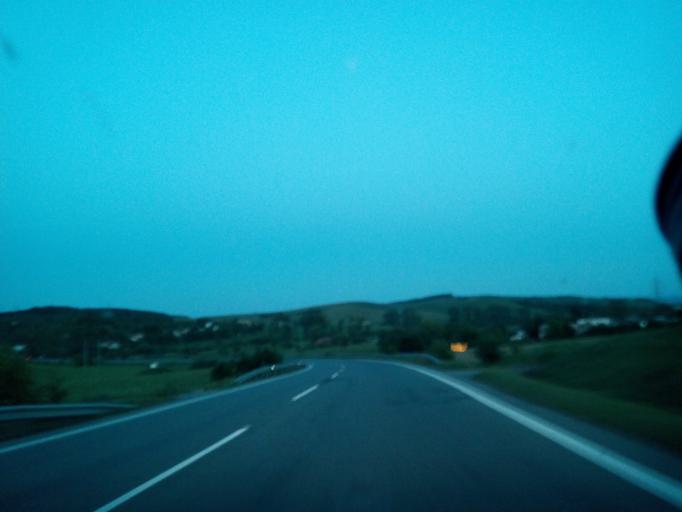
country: SK
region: Banskobystricky
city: Rimavska Sobota
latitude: 48.3892
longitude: 20.0430
